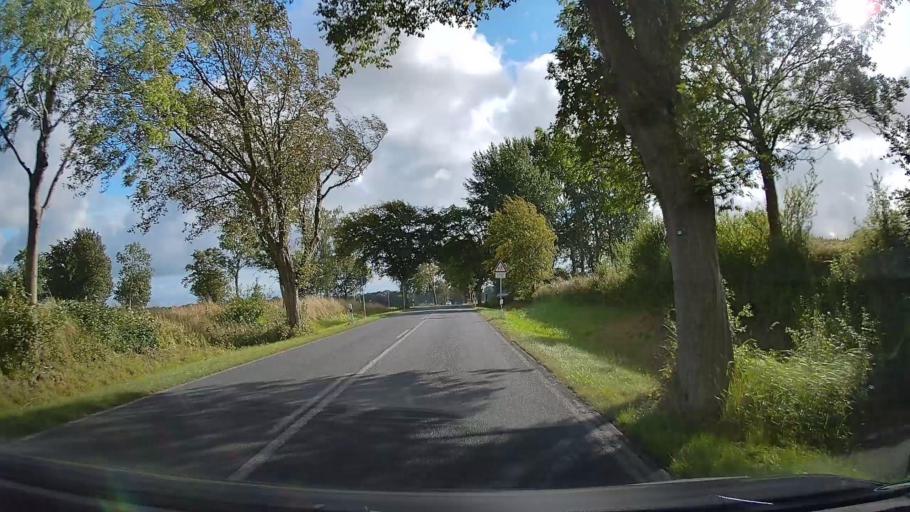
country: DE
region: Mecklenburg-Vorpommern
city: Putbus
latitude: 54.3693
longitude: 13.4791
